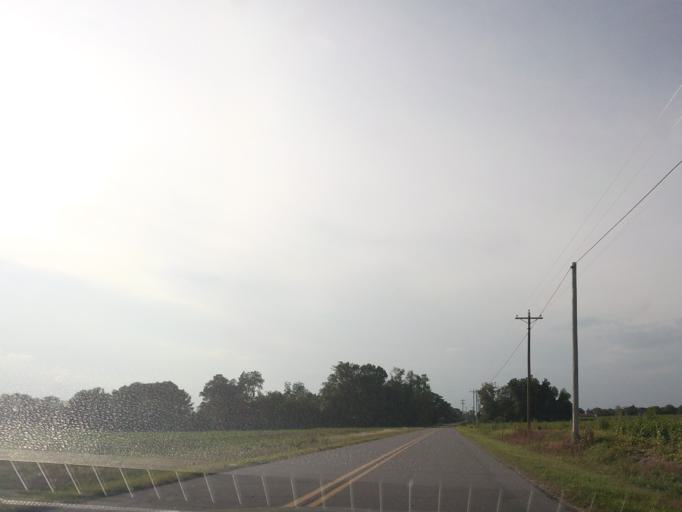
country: US
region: Georgia
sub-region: Bleckley County
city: Cochran
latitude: 32.5002
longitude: -83.2977
